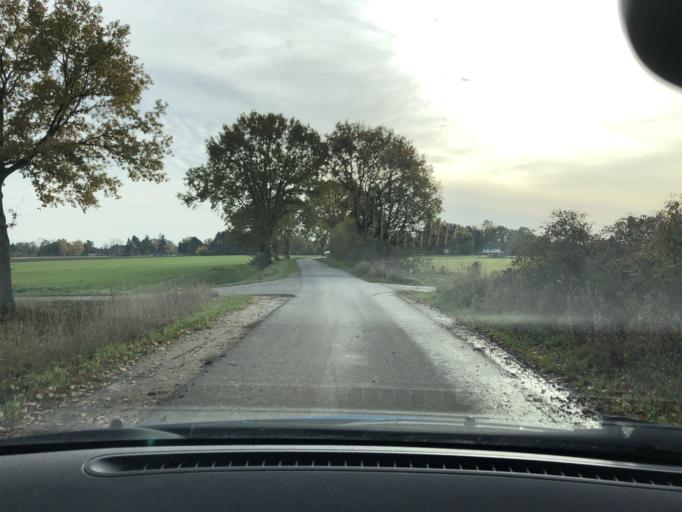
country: DE
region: Lower Saxony
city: Brietlingen
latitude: 53.3566
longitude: 10.4437
